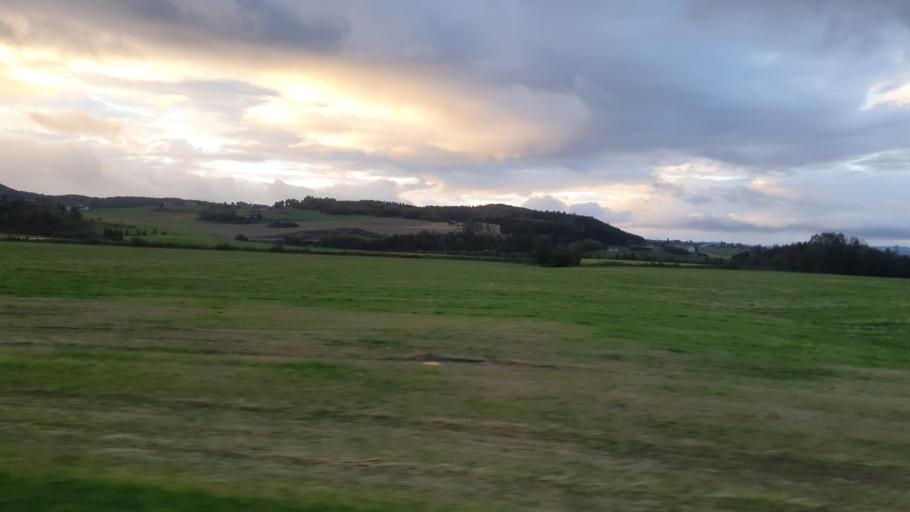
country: NO
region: Nord-Trondelag
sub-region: Levanger
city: Skogn
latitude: 63.6772
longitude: 11.1461
